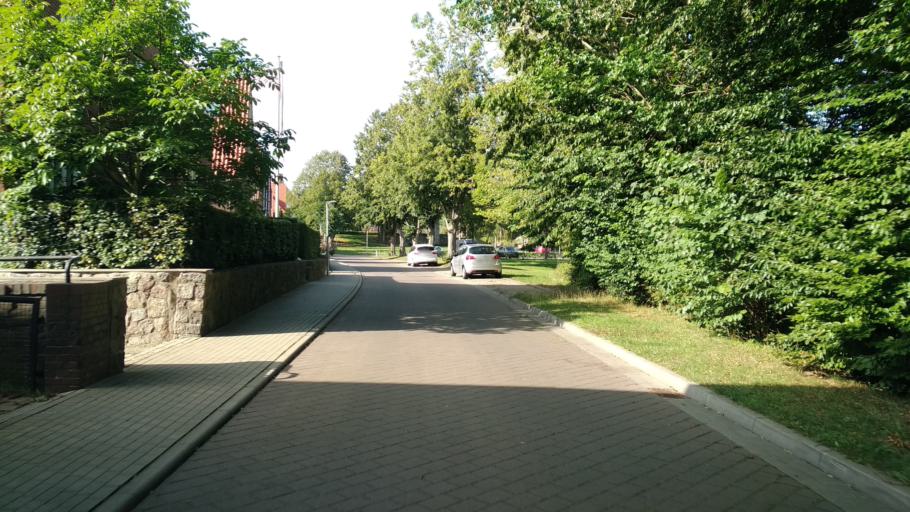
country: DE
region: Schleswig-Holstein
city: Schleswig
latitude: 54.5161
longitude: 9.5548
